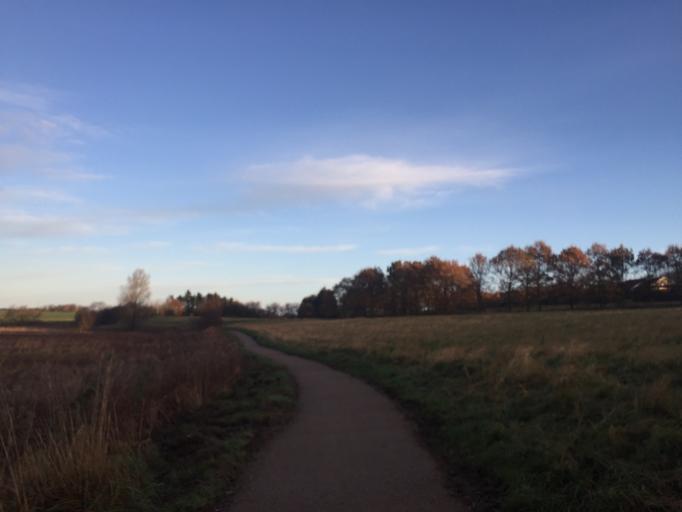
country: DK
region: Zealand
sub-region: Ringsted Kommune
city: Ringsted
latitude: 55.4232
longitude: 11.7757
